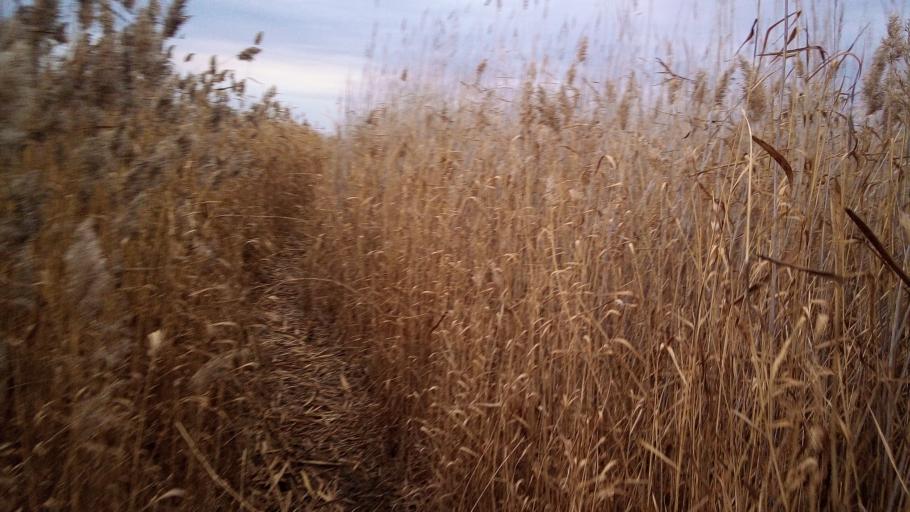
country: RU
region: Chelyabinsk
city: Novosineglazovskiy
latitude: 54.9861
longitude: 61.4032
